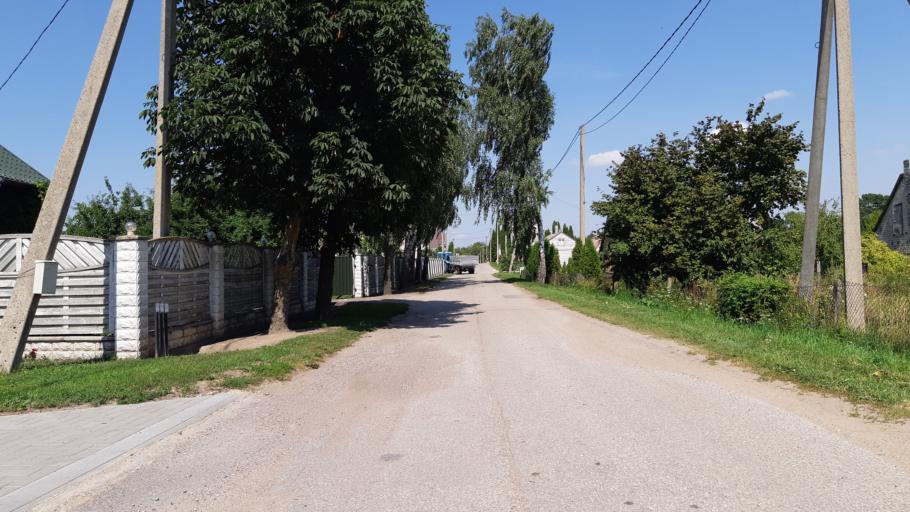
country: LT
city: Virbalis
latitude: 54.6226
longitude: 22.8176
